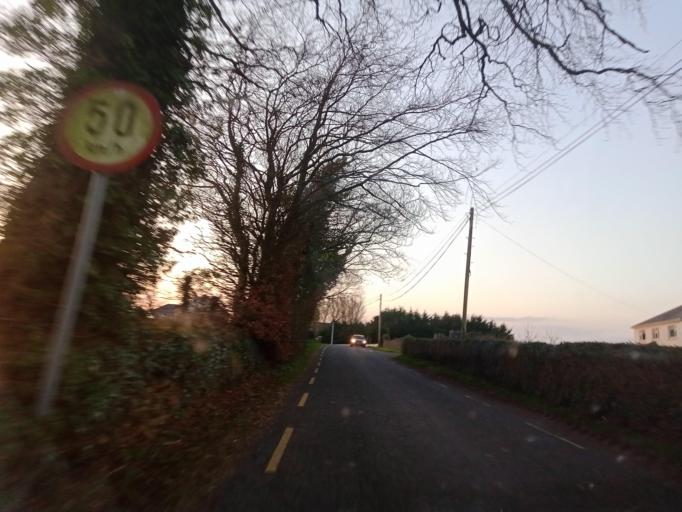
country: IE
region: Leinster
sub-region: Laois
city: Abbeyleix
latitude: 52.9634
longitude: -7.3668
